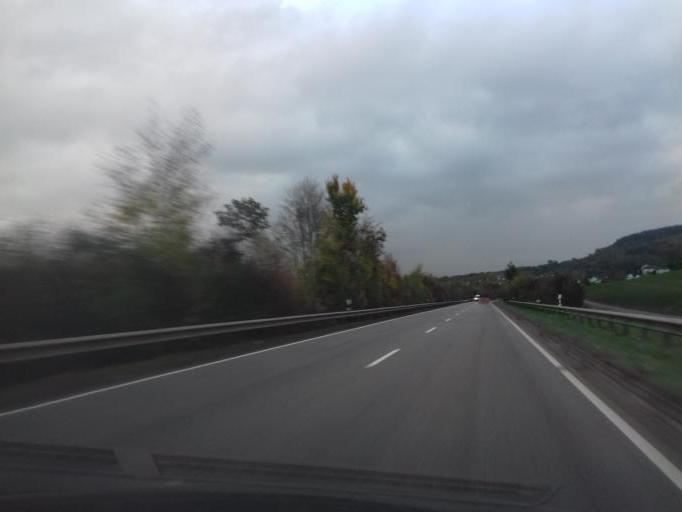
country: DE
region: Rheinland-Pfalz
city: Ayl
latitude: 49.6378
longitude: 6.5480
